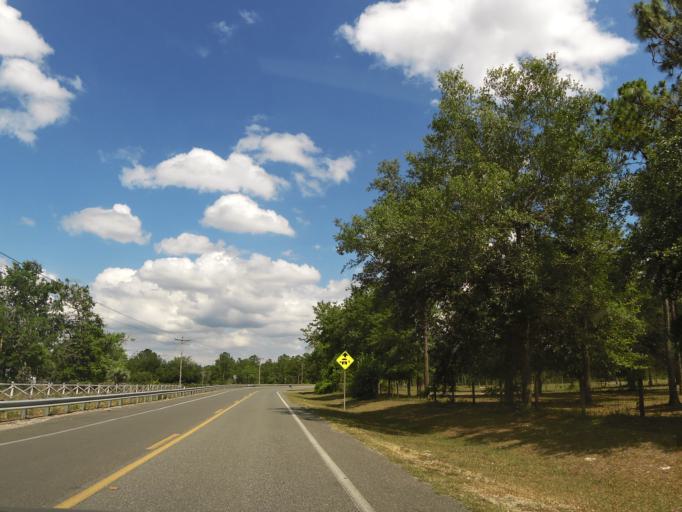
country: US
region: Florida
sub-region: Clay County
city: Keystone Heights
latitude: 29.8673
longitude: -81.9161
